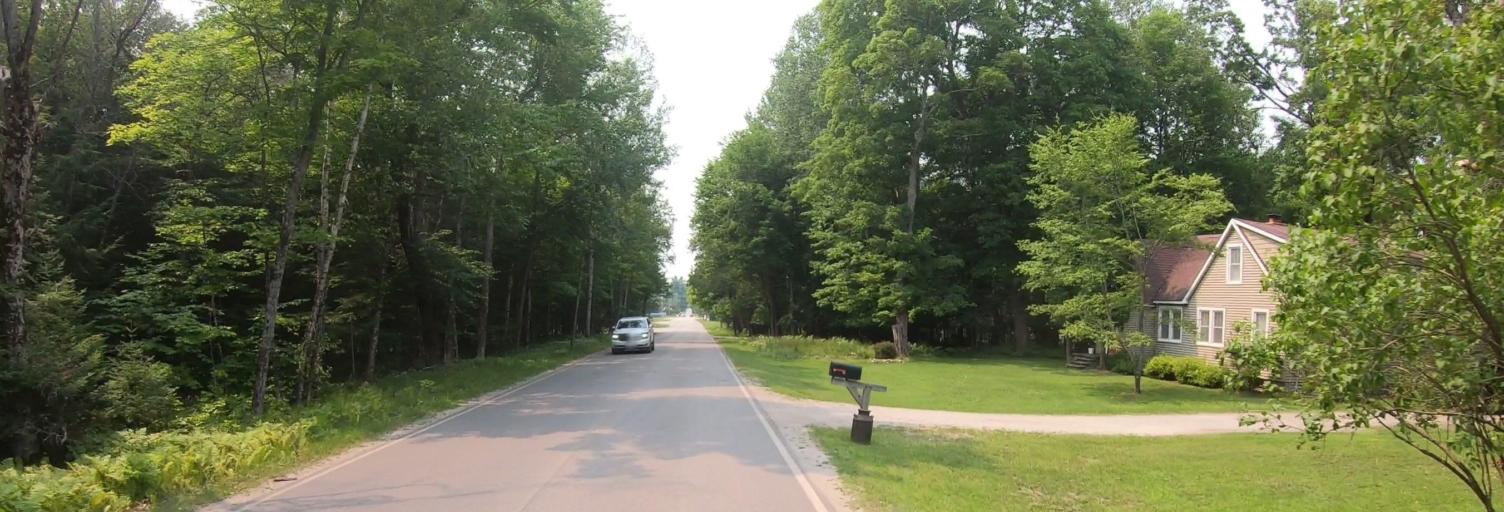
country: CA
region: Ontario
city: Thessalon
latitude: 46.0205
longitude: -83.7352
